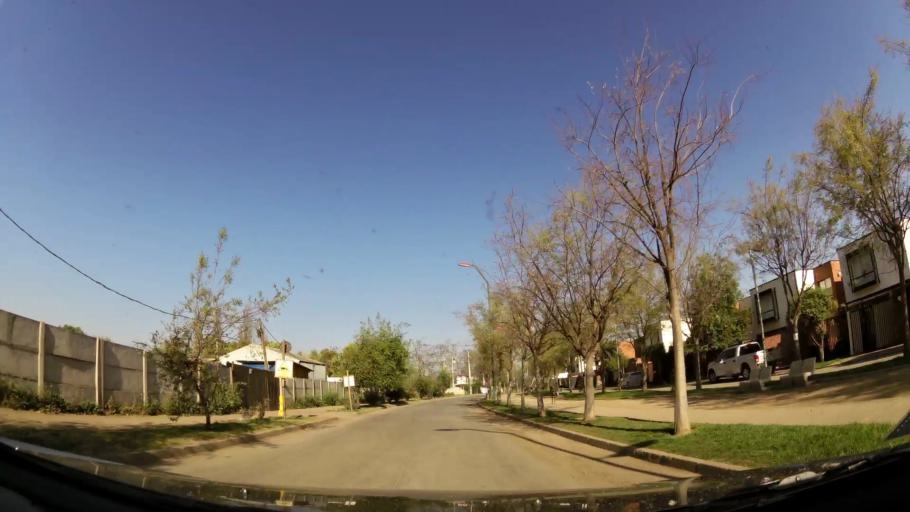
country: CL
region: Santiago Metropolitan
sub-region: Provincia de Chacabuco
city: Chicureo Abajo
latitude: -33.3665
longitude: -70.6686
